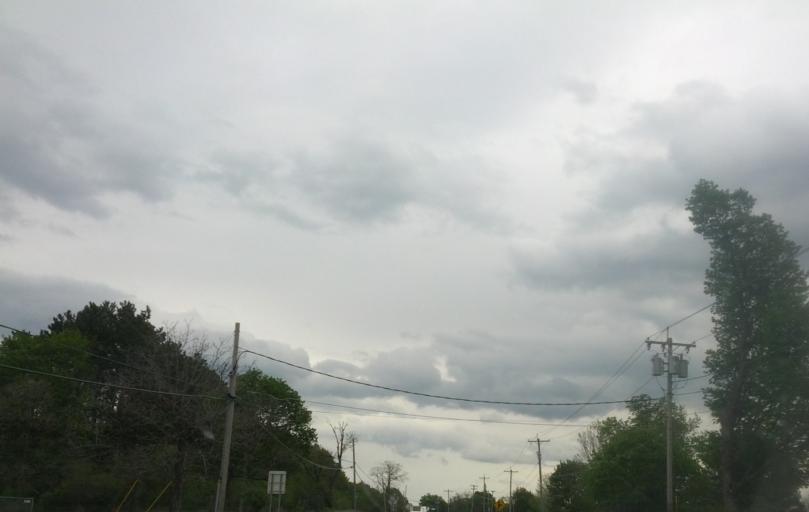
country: US
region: New York
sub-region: Onondaga County
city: Fayetteville
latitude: 42.9903
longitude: -76.0625
